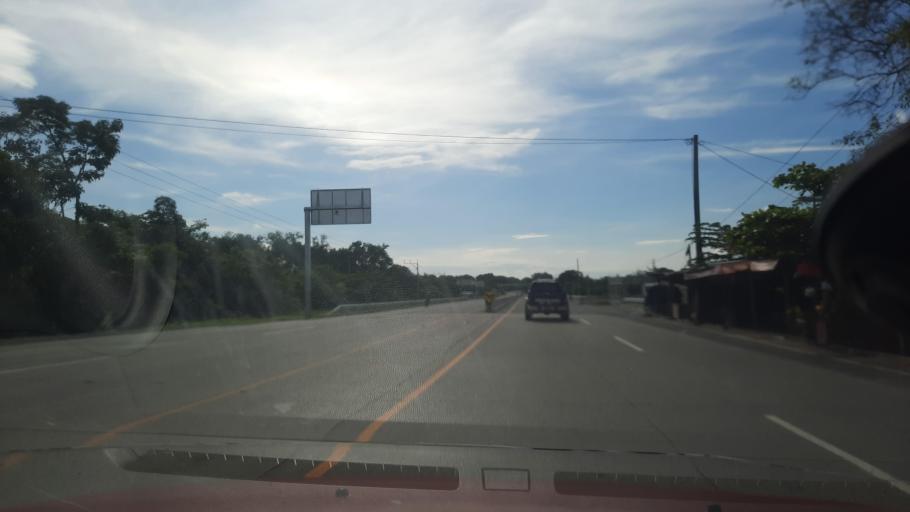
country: SV
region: La Paz
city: El Rosario
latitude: 13.4788
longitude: -89.0640
